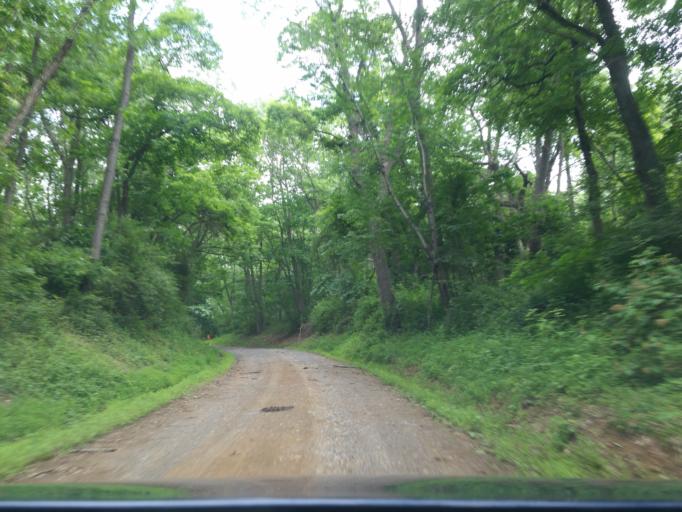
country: US
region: Pennsylvania
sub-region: Lebanon County
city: Jonestown
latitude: 40.4260
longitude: -76.5296
